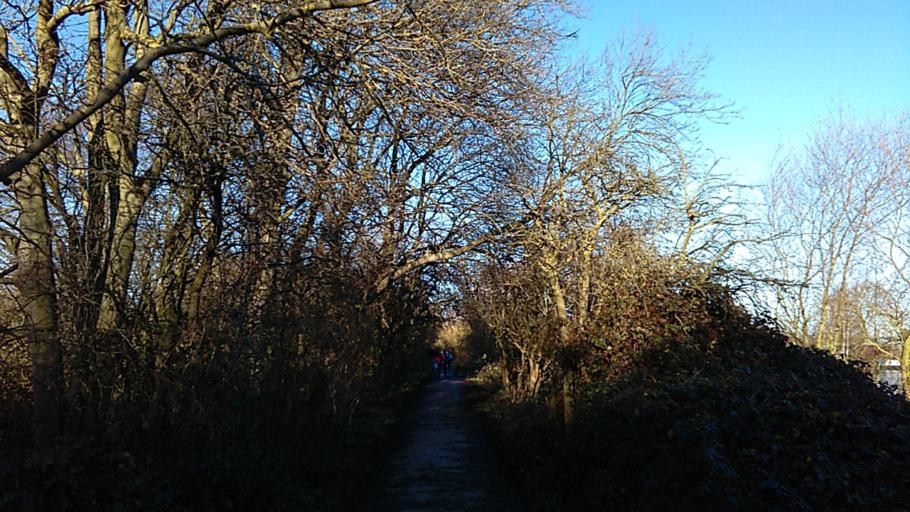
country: GB
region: England
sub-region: Nottinghamshire
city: Gotham
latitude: 52.9075
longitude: -1.2145
